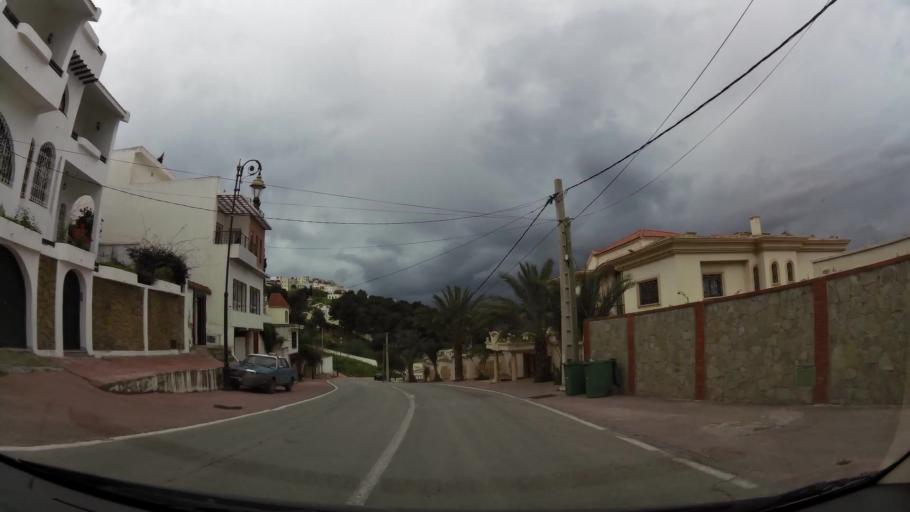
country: MA
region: Tanger-Tetouan
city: Tetouan
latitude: 35.5529
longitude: -5.3716
